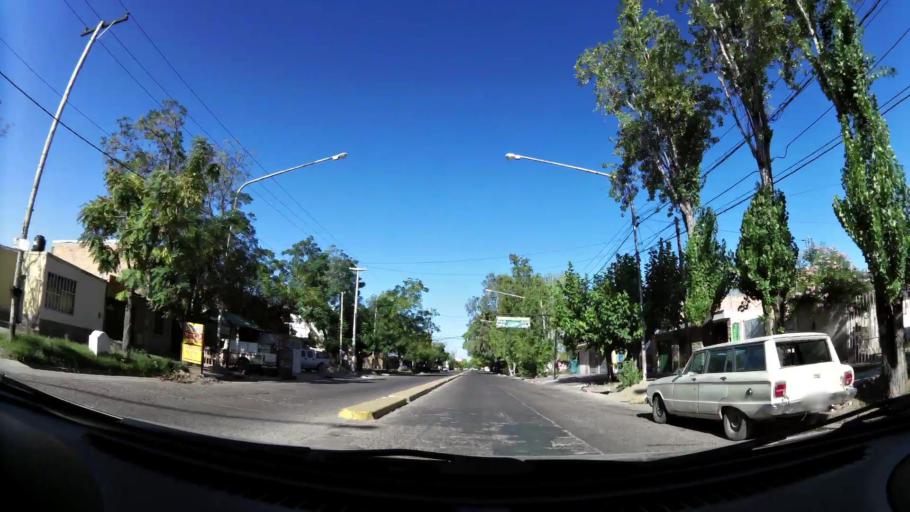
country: AR
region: Mendoza
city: Las Heras
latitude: -32.8421
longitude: -68.8153
